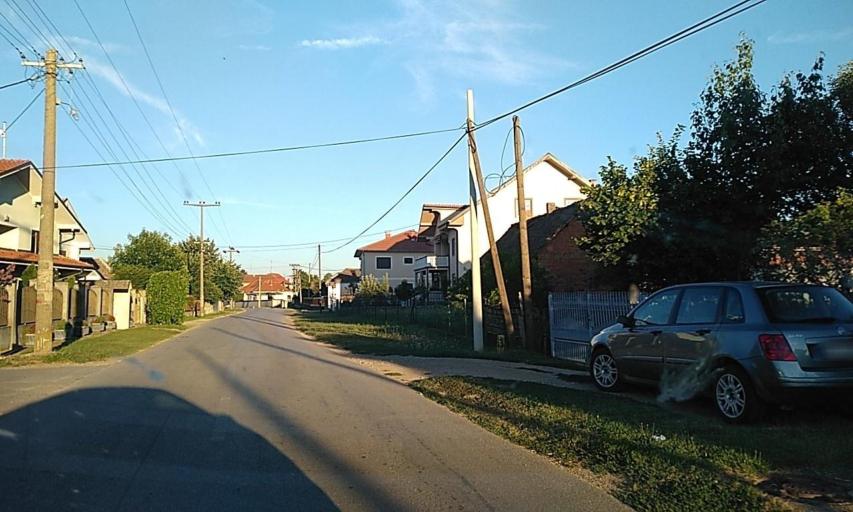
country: RS
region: Central Serbia
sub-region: Branicevski Okrug
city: Malo Crnice
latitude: 44.6938
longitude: 21.3528
